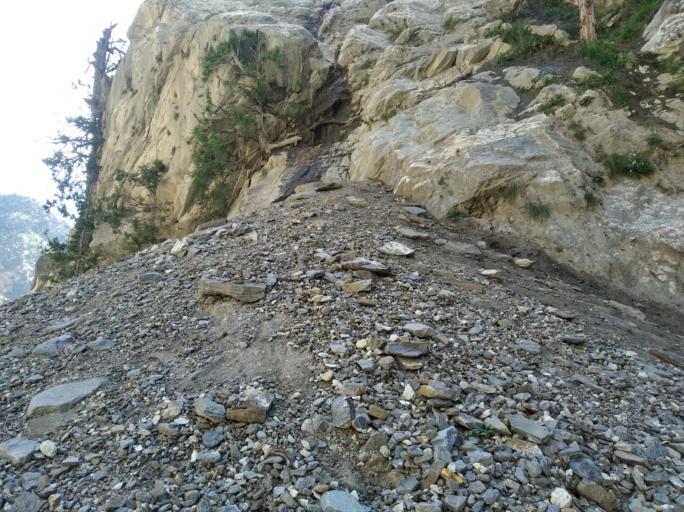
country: NP
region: Western Region
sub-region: Dhawalagiri Zone
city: Jomsom
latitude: 28.8975
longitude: 83.0624
